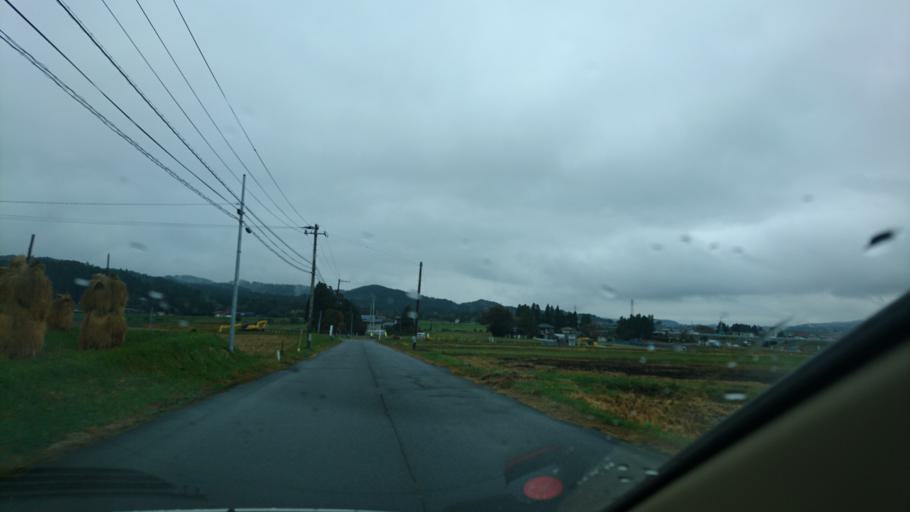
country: JP
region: Iwate
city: Ichinoseki
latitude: 38.9724
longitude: 141.1093
